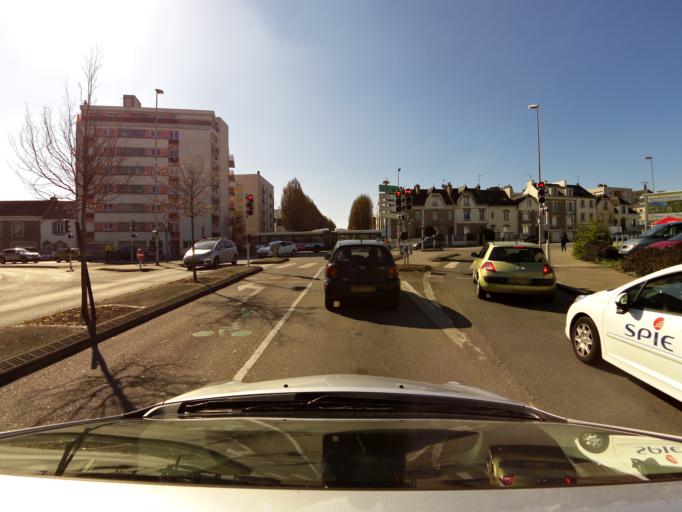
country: FR
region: Brittany
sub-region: Departement du Morbihan
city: Lorient
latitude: 47.7442
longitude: -3.3813
